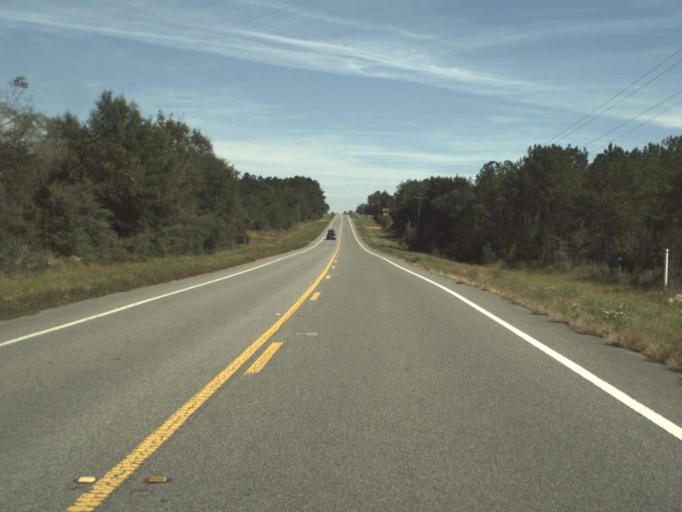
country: US
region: Florida
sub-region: Washington County
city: Chipley
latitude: 30.5671
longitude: -85.6065
